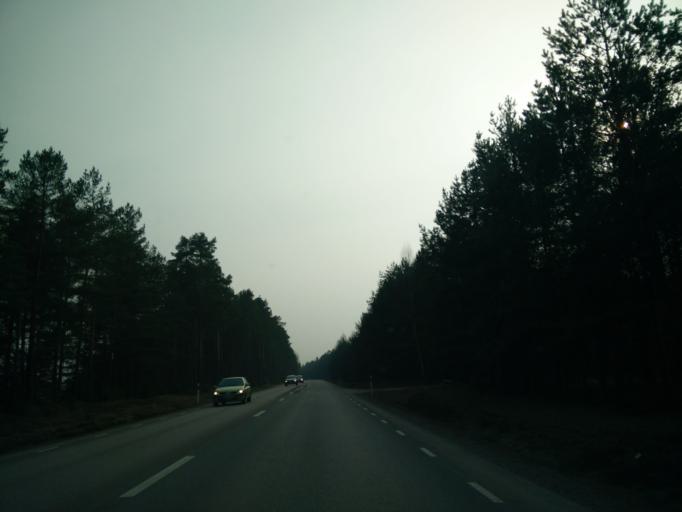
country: SE
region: Vaermland
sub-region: Forshaga Kommun
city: Forshaga
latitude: 59.4878
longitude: 13.4195
